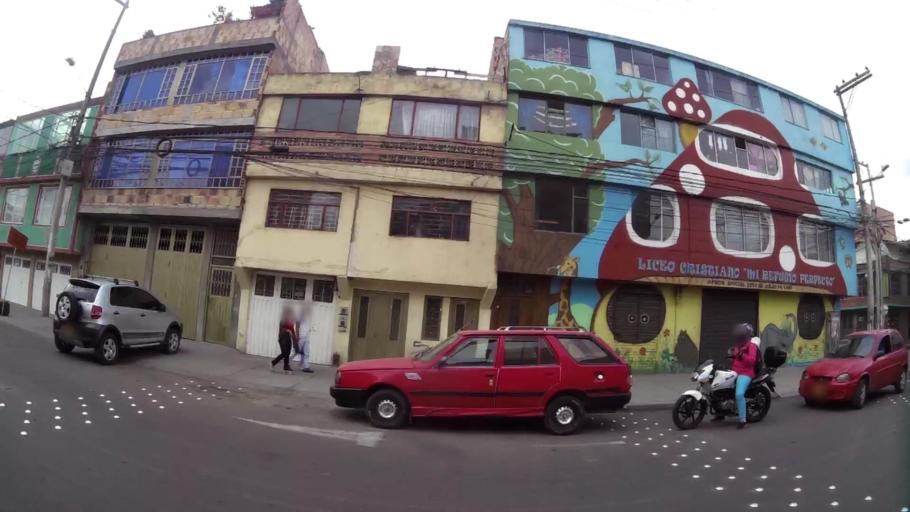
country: CO
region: Cundinamarca
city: Soacha
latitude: 4.6399
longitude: -74.1628
